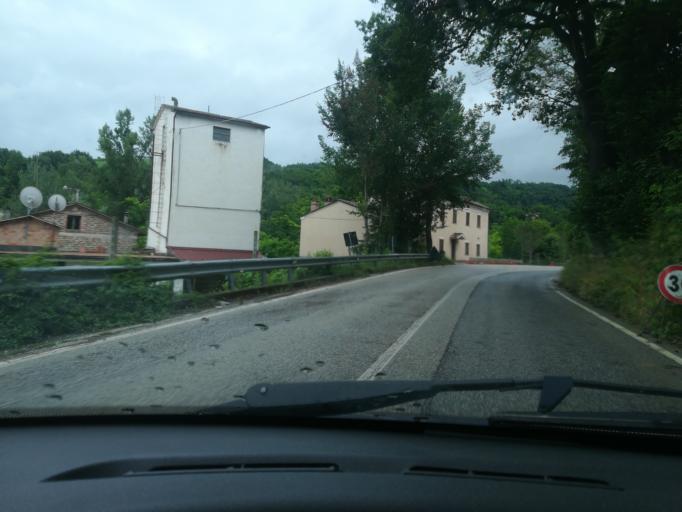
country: IT
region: The Marches
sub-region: Provincia di Macerata
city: San Ginesio
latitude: 43.0997
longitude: 13.3435
